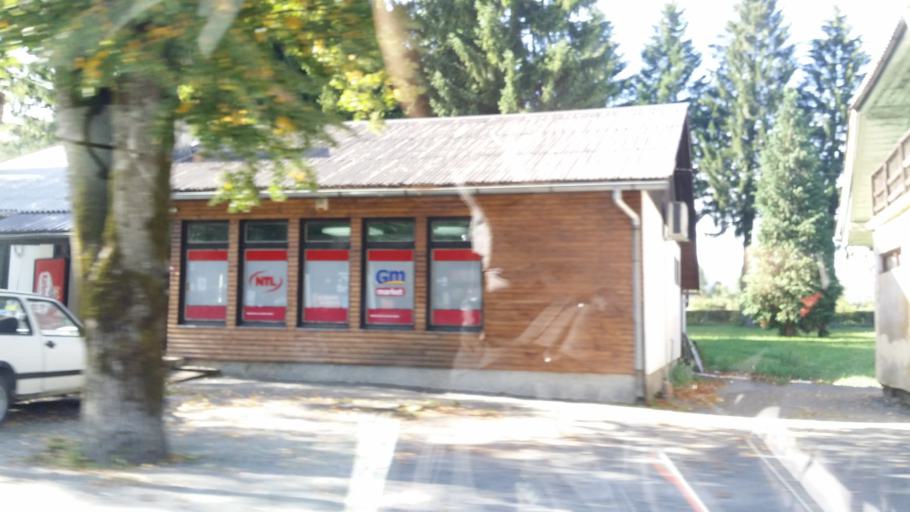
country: HR
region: Primorsko-Goranska
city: Vrbovsko
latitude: 45.2308
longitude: 15.0406
